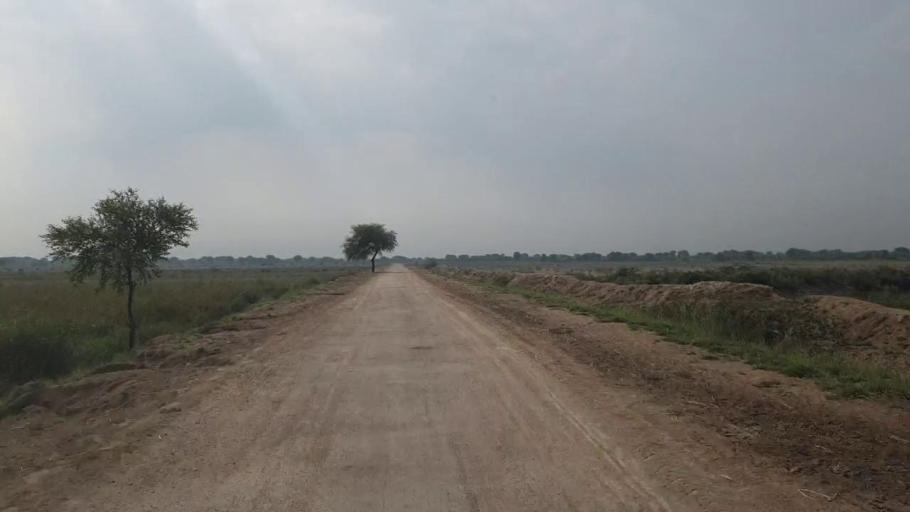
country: PK
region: Sindh
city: Talhar
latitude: 24.8668
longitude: 68.8357
